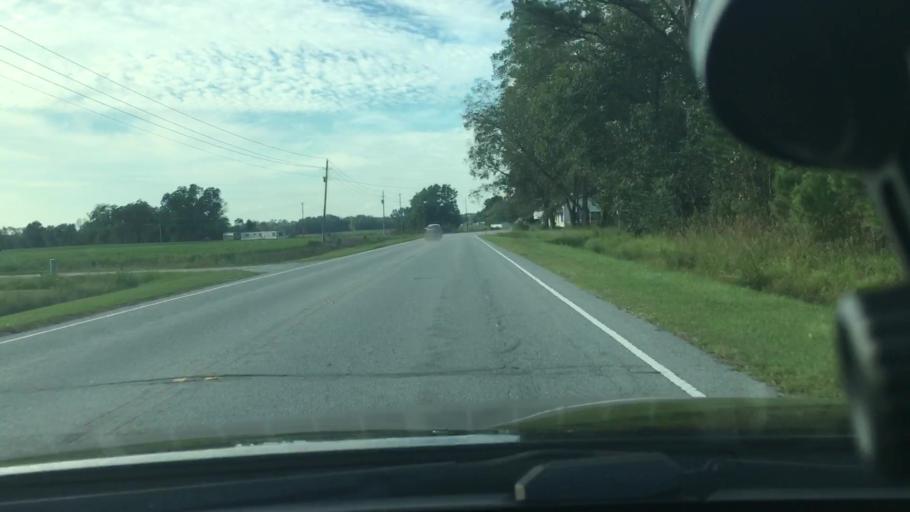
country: US
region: North Carolina
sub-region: Craven County
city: Vanceboro
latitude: 35.4216
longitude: -77.2590
